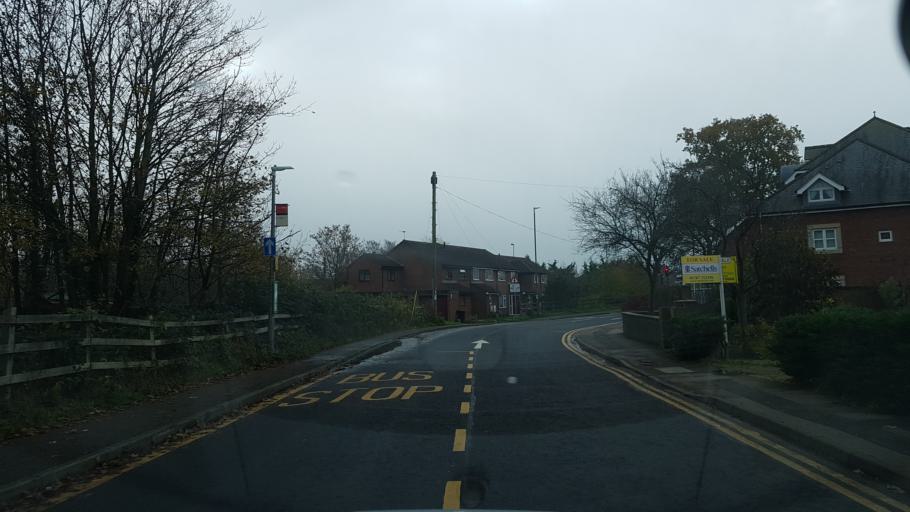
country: GB
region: England
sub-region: Central Bedfordshire
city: Biggleswade
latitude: 52.0903
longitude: -0.2621
